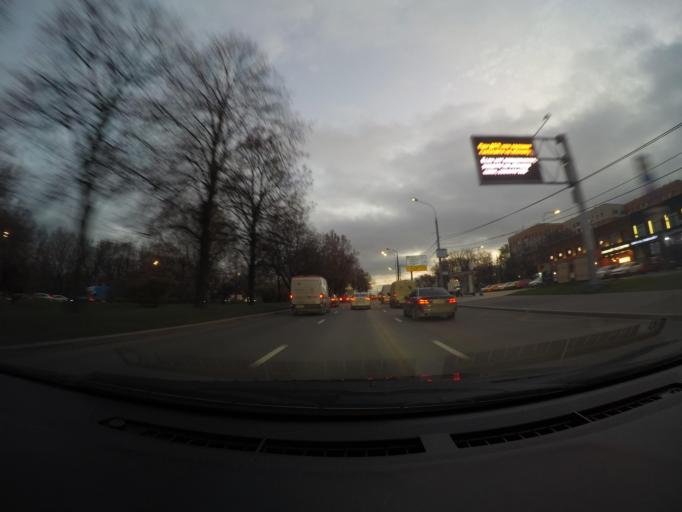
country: RU
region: Moscow
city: Kolomenskoye
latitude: 55.6696
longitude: 37.6615
